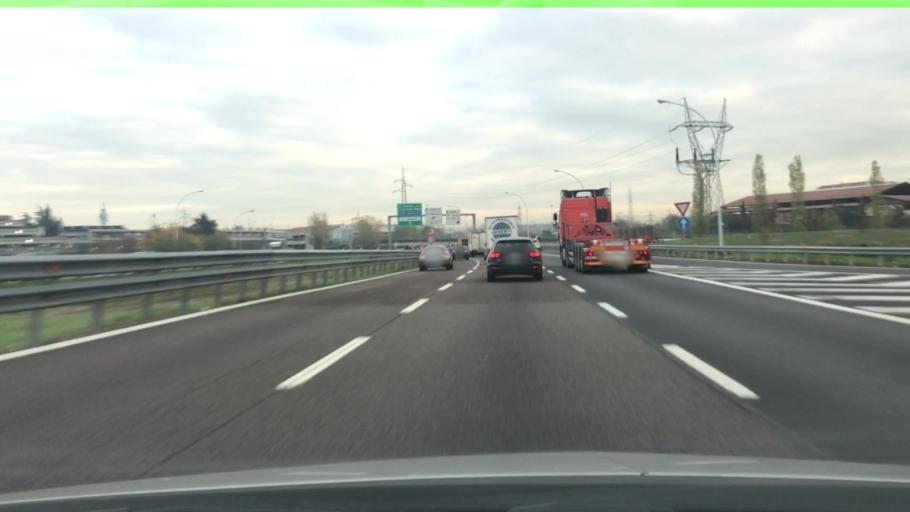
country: IT
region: Lombardy
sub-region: Citta metropolitana di Milano
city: Vimodrone
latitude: 45.5076
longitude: 9.2611
